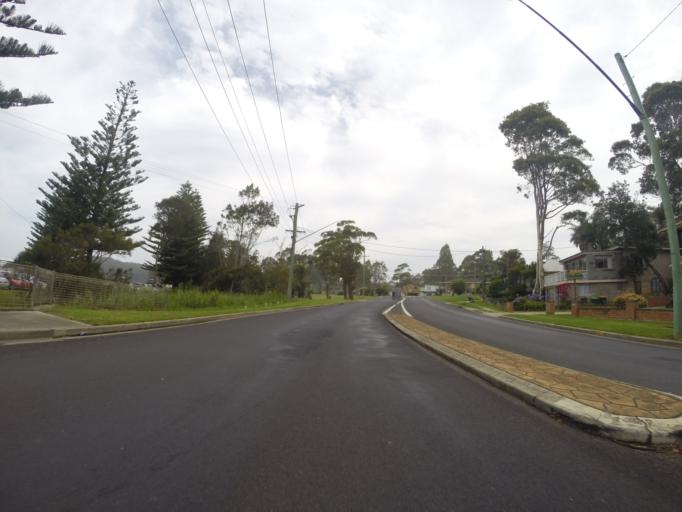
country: AU
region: New South Wales
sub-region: Eurobodalla
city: Batemans Bay
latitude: -35.7572
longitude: 150.2098
